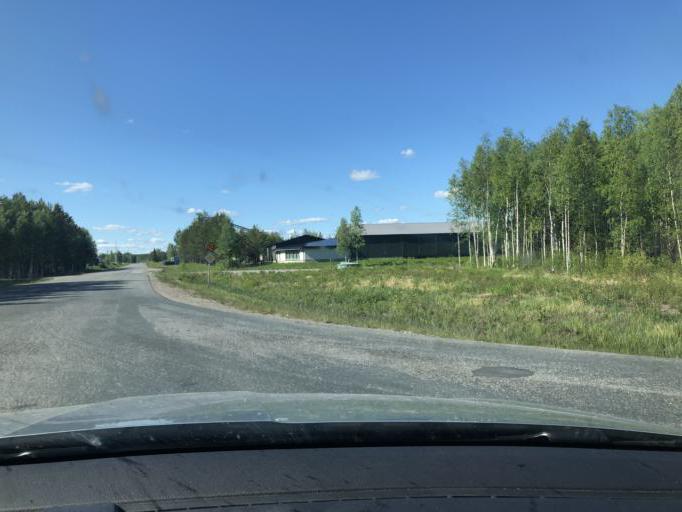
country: SE
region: Norrbotten
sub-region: Kalix Kommun
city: Kalix
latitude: 65.8467
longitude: 23.1996
